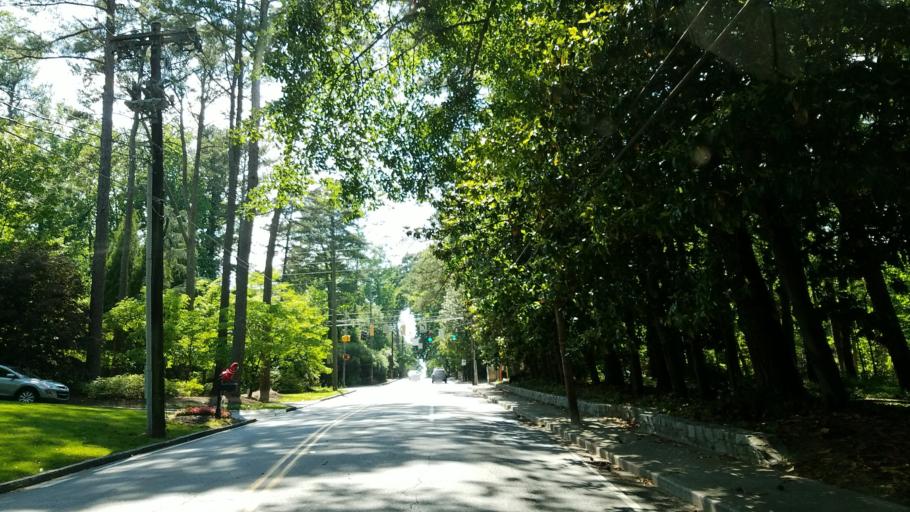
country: US
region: Georgia
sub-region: Cobb County
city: Vinings
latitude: 33.8287
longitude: -84.4066
